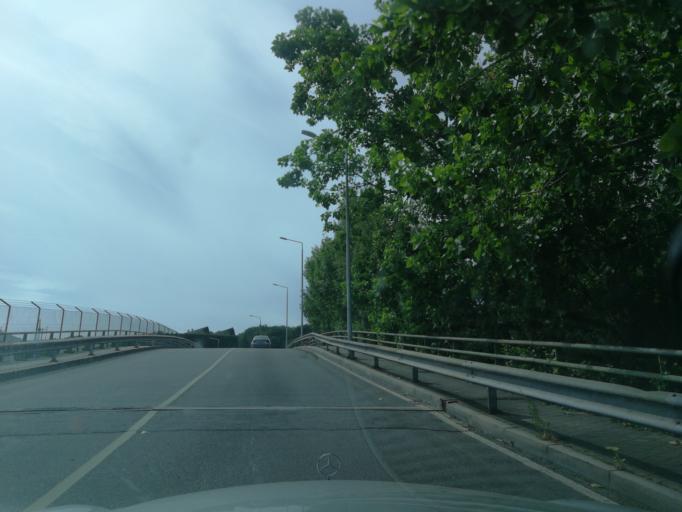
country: PT
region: Braga
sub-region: Vila Nova de Famalicao
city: Calendario
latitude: 41.4073
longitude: -8.5277
